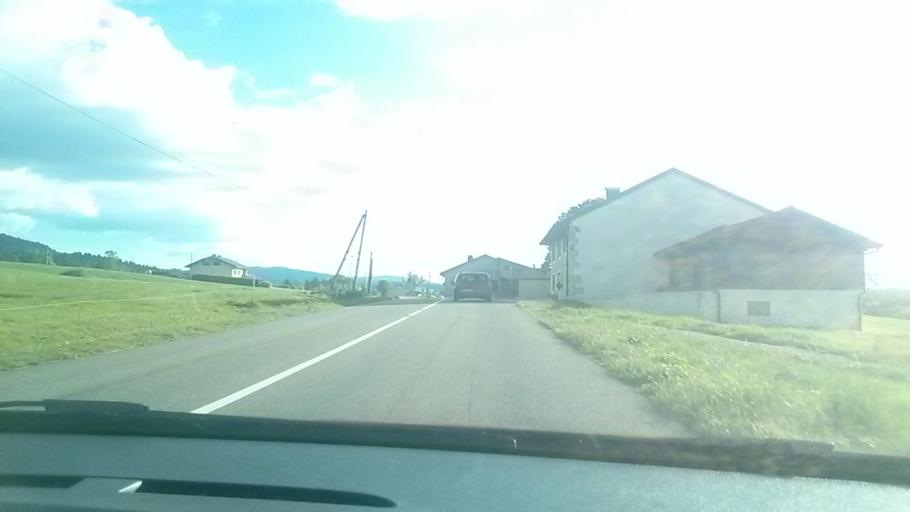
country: FR
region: Franche-Comte
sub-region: Departement du Jura
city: Les Rousses
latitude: 46.5055
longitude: 6.1048
